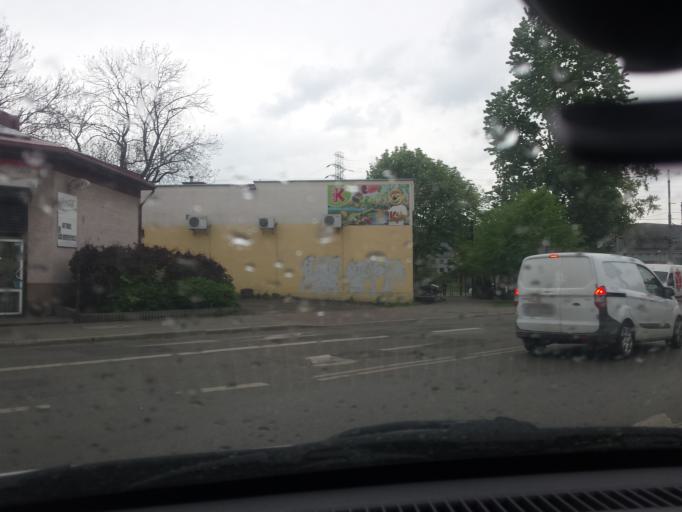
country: PL
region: Silesian Voivodeship
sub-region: Katowice
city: Katowice
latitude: 50.2630
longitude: 19.0034
